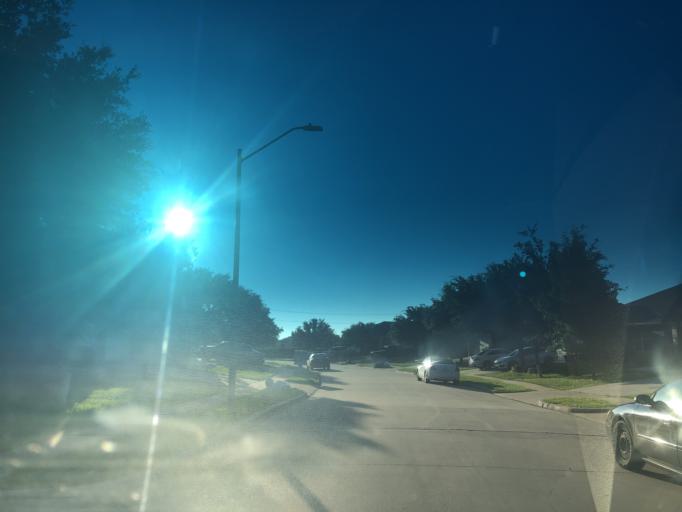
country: US
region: Texas
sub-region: Dallas County
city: Grand Prairie
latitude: 32.7018
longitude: -97.0200
